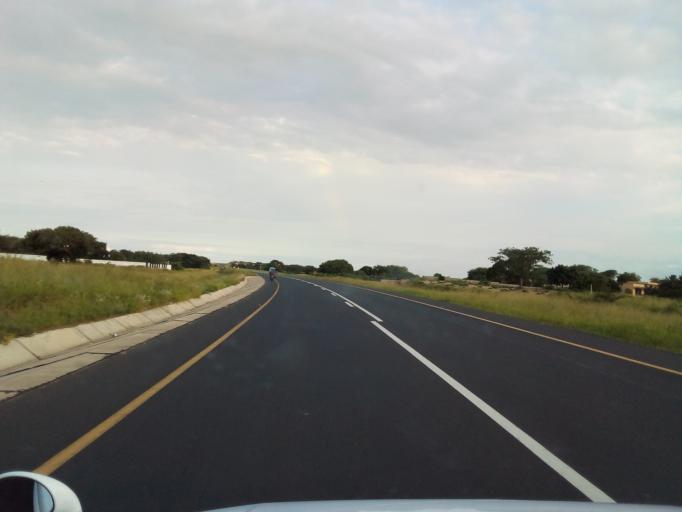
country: MZ
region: Maputo City
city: Maputo
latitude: -26.0359
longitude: 32.5557
